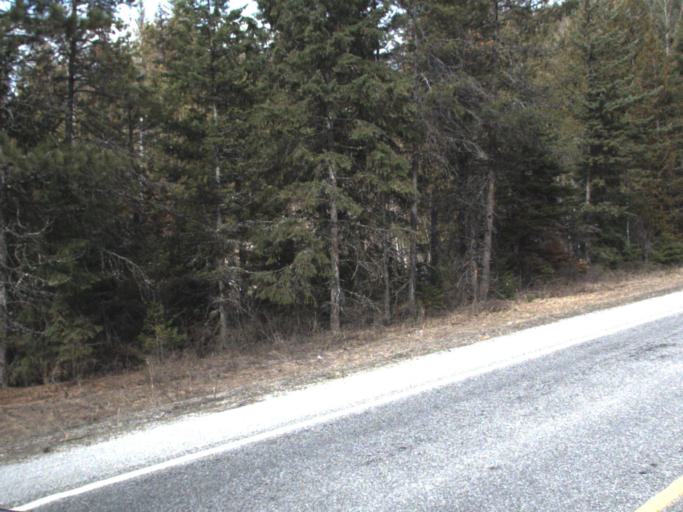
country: US
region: Washington
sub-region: Pend Oreille County
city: Newport
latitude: 48.4166
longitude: -117.3171
